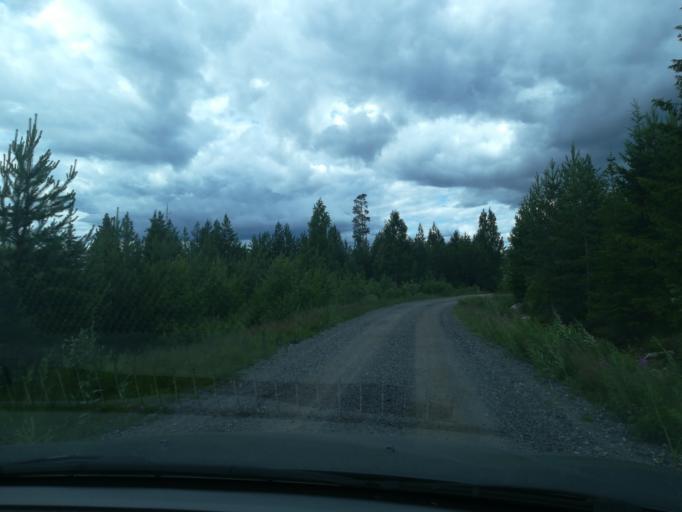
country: FI
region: Southern Savonia
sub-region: Mikkeli
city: Mikkeli
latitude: 61.6722
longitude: 27.1181
